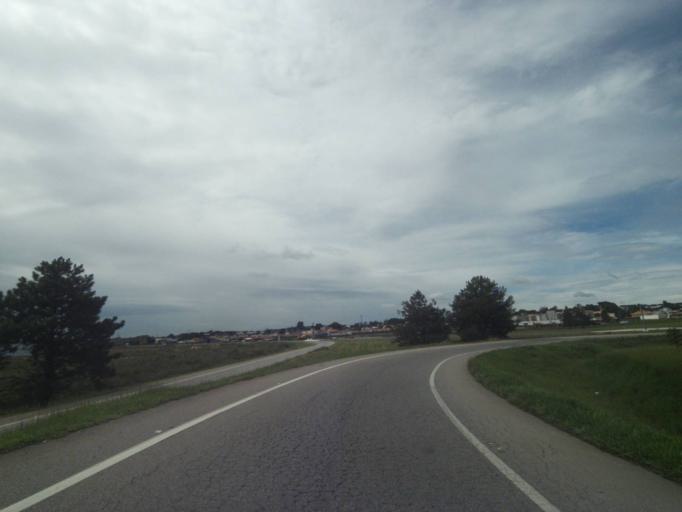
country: BR
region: Parana
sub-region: Sao Jose Dos Pinhais
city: Sao Jose dos Pinhais
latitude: -25.5108
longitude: -49.1258
